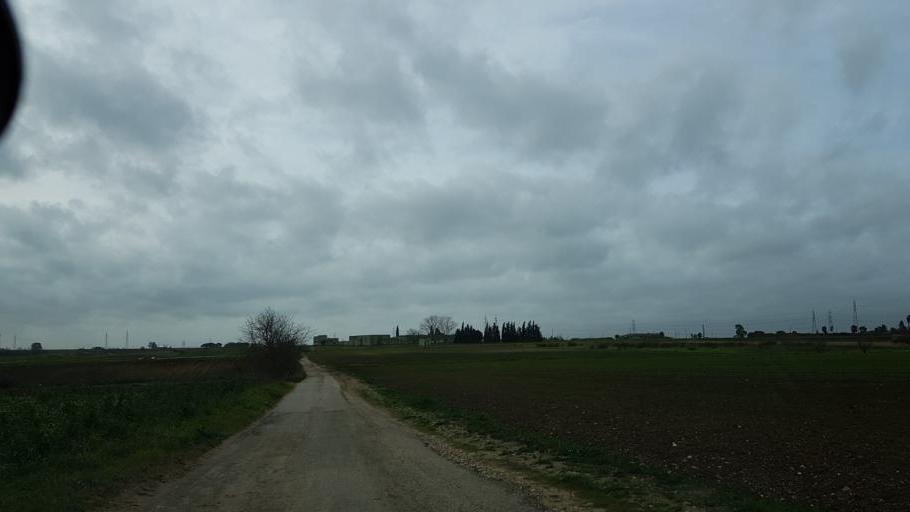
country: IT
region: Apulia
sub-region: Provincia di Brindisi
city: La Rosa
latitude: 40.5950
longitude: 17.9178
